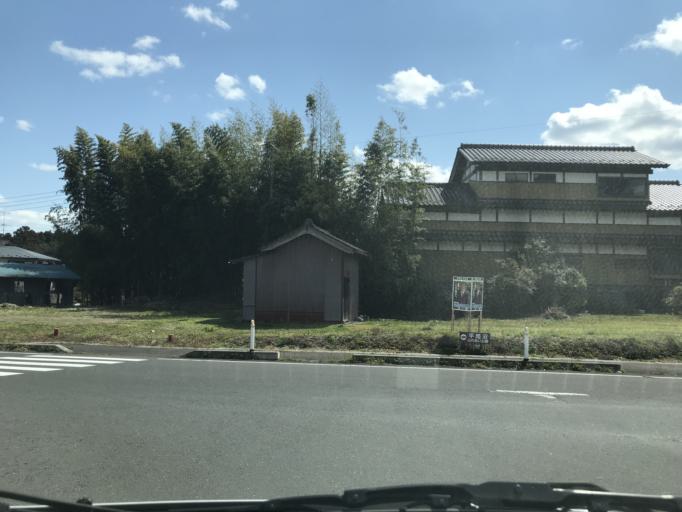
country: JP
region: Miyagi
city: Wakuya
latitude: 38.6232
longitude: 141.2248
